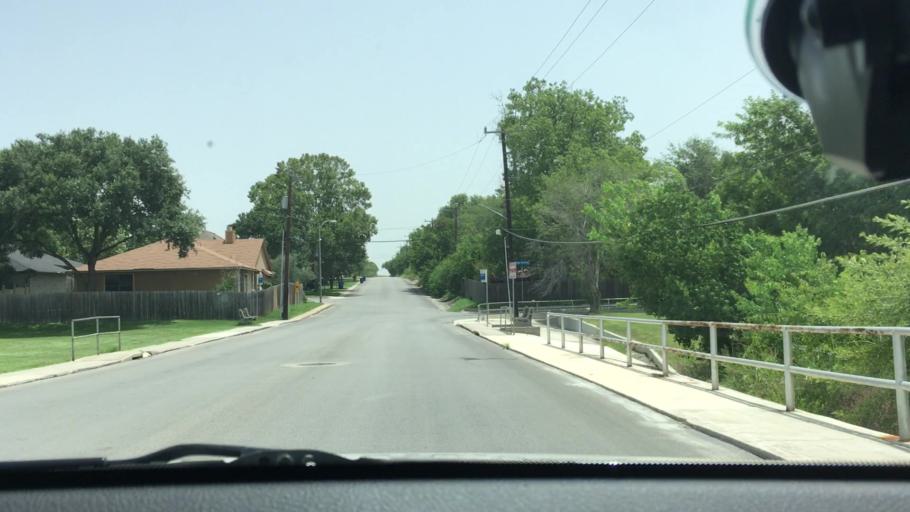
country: US
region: Texas
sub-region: Bexar County
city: Live Oak
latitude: 29.5757
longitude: -98.3660
